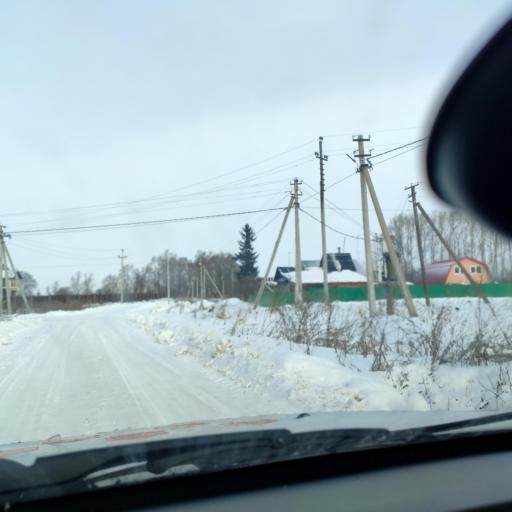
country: RU
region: Bashkortostan
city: Mikhaylovka
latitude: 54.8706
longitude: 55.7503
